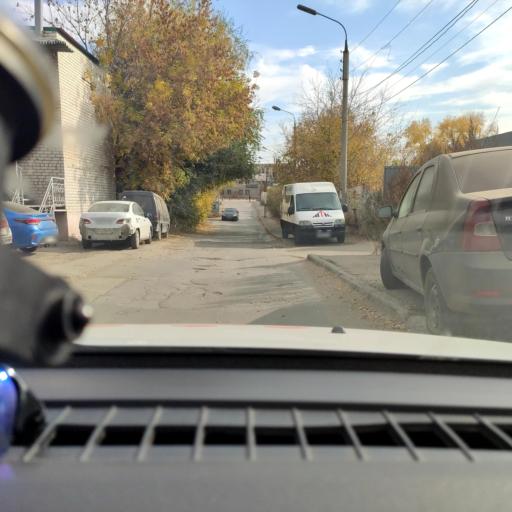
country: RU
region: Samara
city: Samara
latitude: 53.1815
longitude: 50.1108
